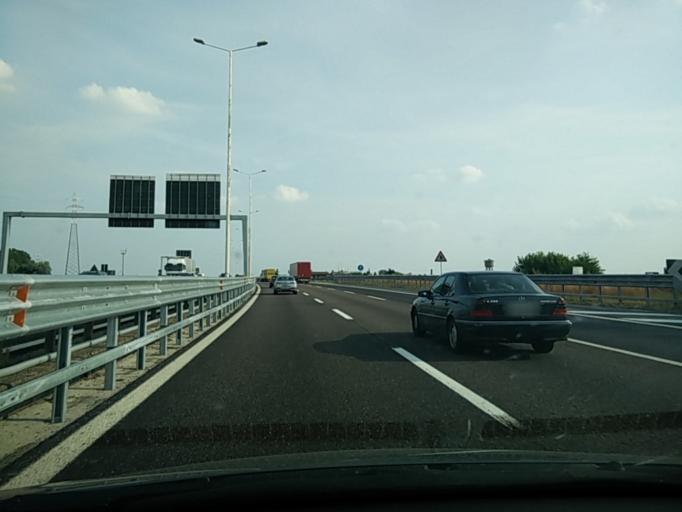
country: IT
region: Lombardy
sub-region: Citta metropolitana di Milano
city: Figino
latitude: 45.4906
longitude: 9.0665
